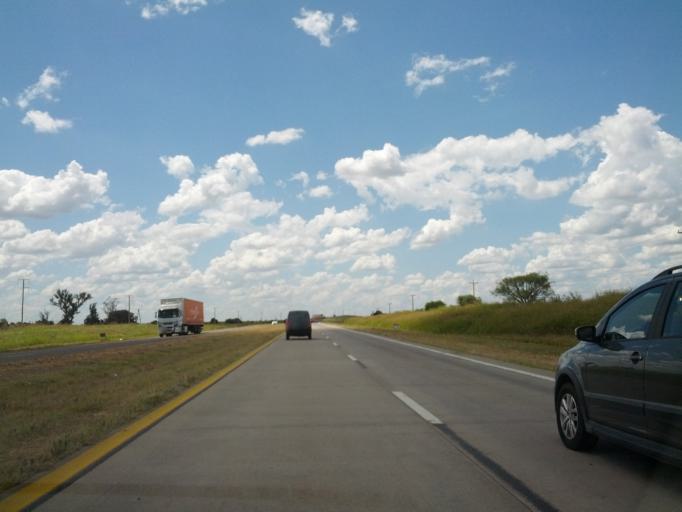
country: AR
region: Entre Rios
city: Gualeguaychu
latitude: -32.9210
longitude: -58.5669
